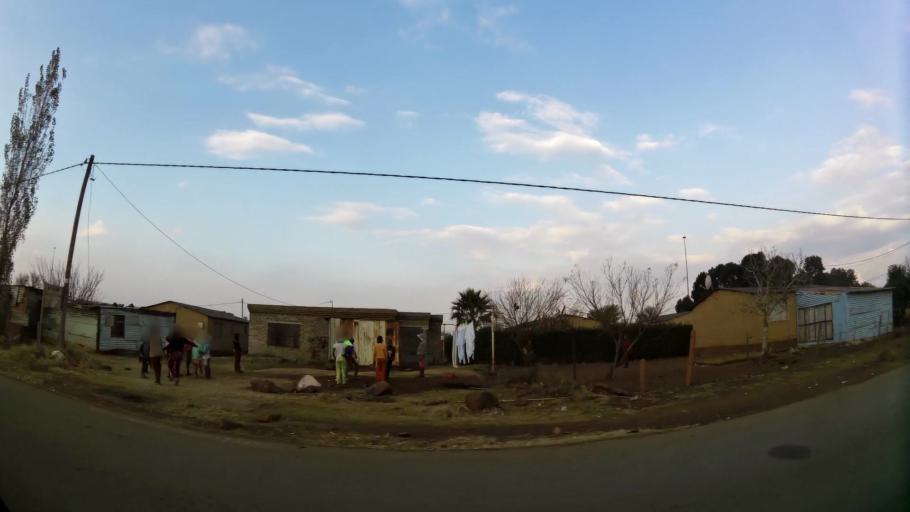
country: ZA
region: Gauteng
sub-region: City of Johannesburg Metropolitan Municipality
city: Orange Farm
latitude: -26.5468
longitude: 27.8334
